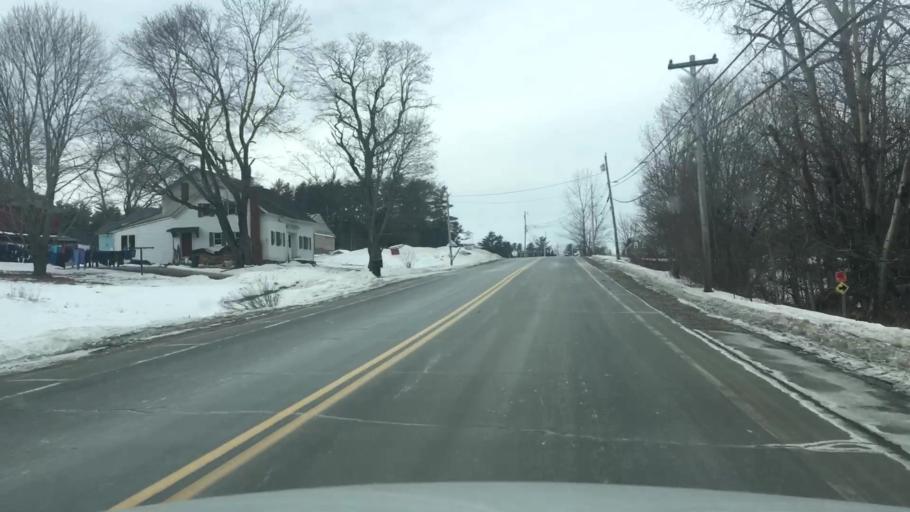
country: US
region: Maine
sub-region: Lincoln County
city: Whitefield
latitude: 44.2227
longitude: -69.5948
